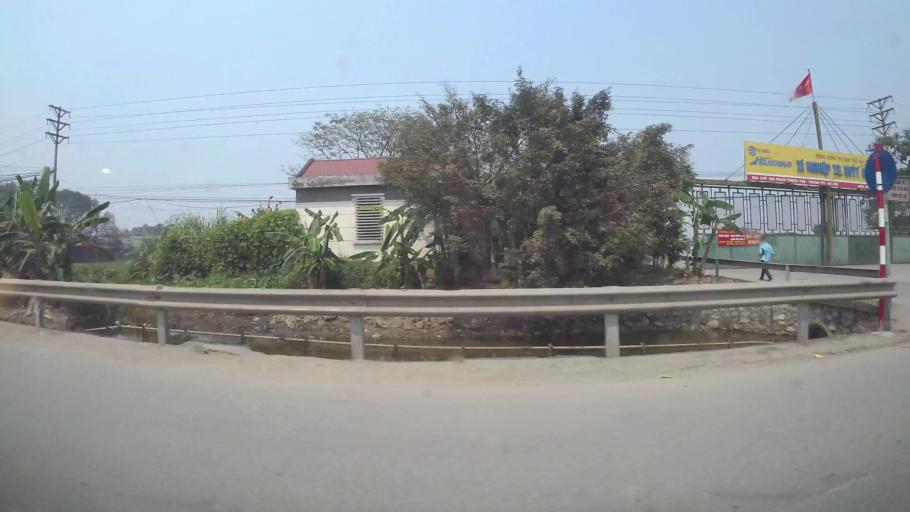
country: VN
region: Ha Noi
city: Van Dien
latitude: 20.9548
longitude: 105.8124
